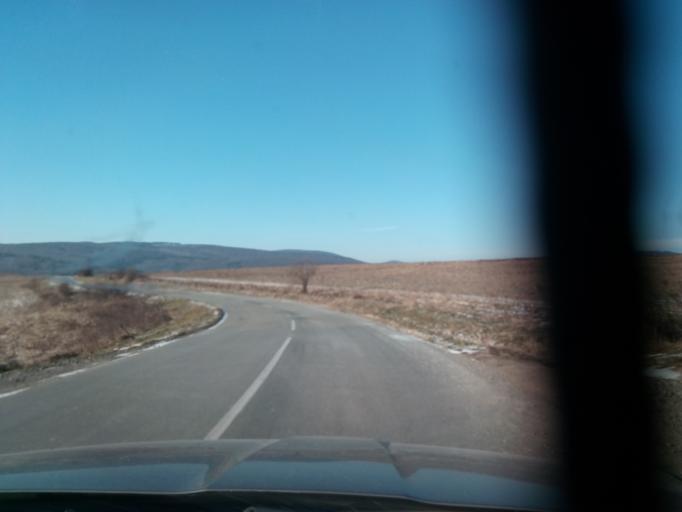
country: SK
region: Kosicky
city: Kosice
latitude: 48.7088
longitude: 21.1679
